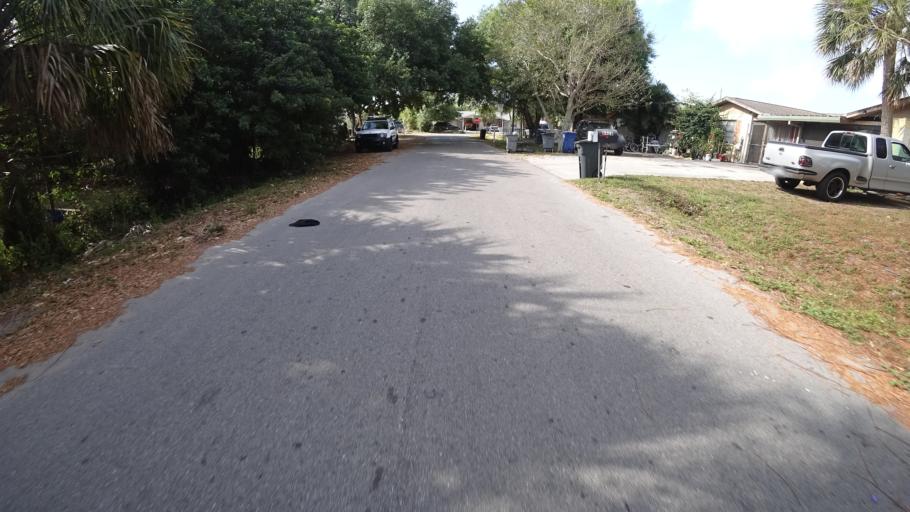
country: US
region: Florida
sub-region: Manatee County
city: Whitfield
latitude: 27.4265
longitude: -82.5709
